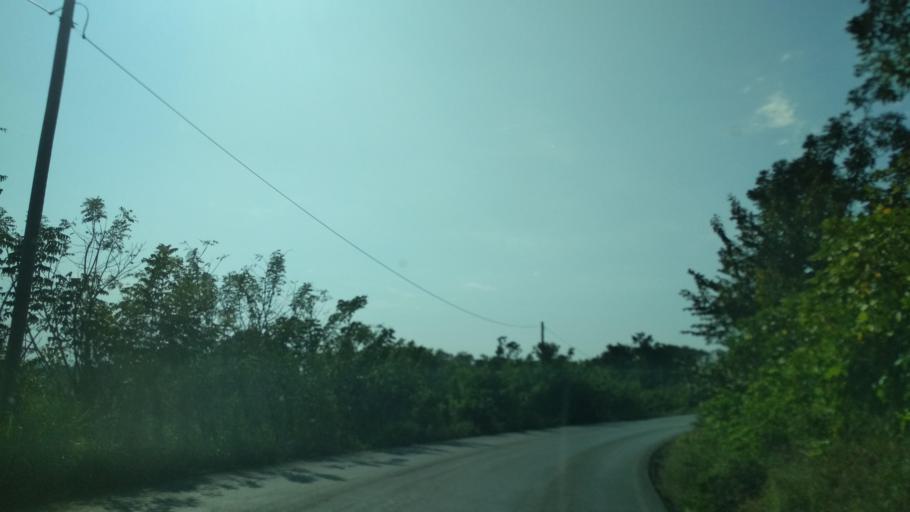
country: MM
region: Shan
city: Taunggyi
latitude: 20.3840
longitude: 97.2877
